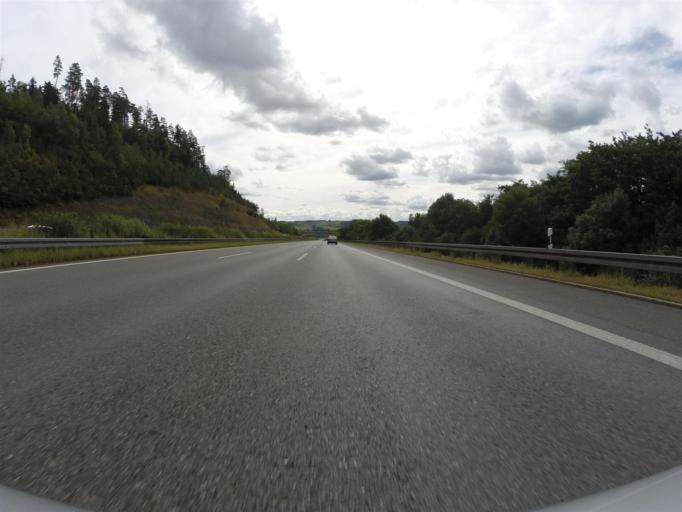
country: DE
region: Bavaria
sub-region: Upper Franconia
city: Himmelkron
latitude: 50.0702
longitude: 11.6269
